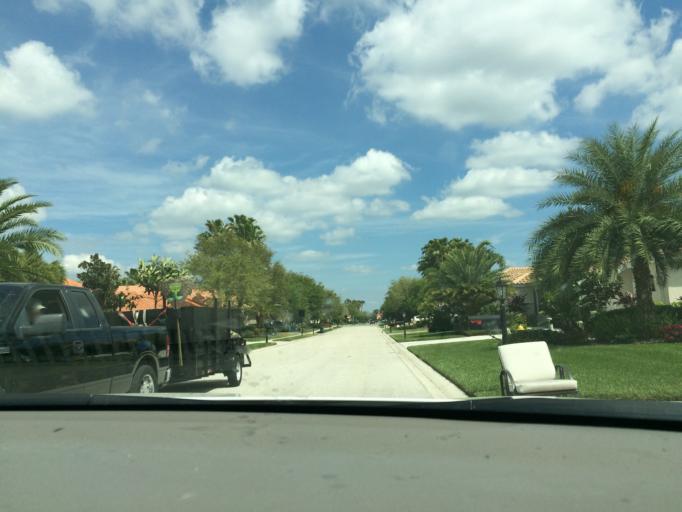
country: US
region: Florida
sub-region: Manatee County
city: Ellenton
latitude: 27.5143
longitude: -82.4375
